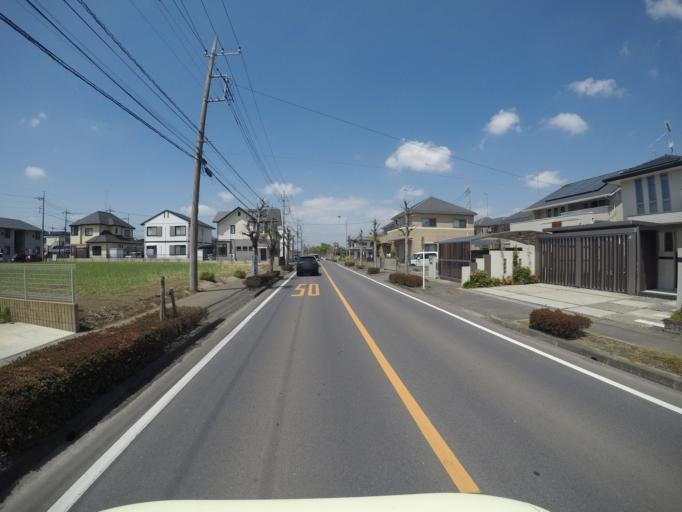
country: JP
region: Tochigi
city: Mibu
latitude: 36.3831
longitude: 139.8382
